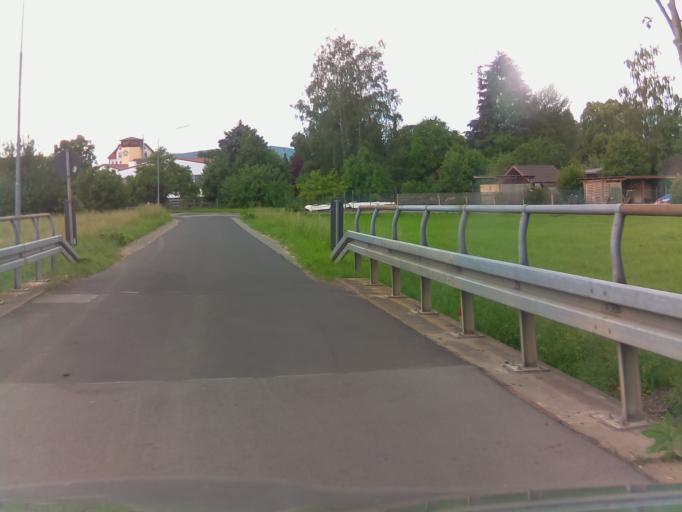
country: DE
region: Bavaria
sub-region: Regierungsbezirk Unterfranken
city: Sondheim vor der Rhoen
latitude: 50.4822
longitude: 10.1826
